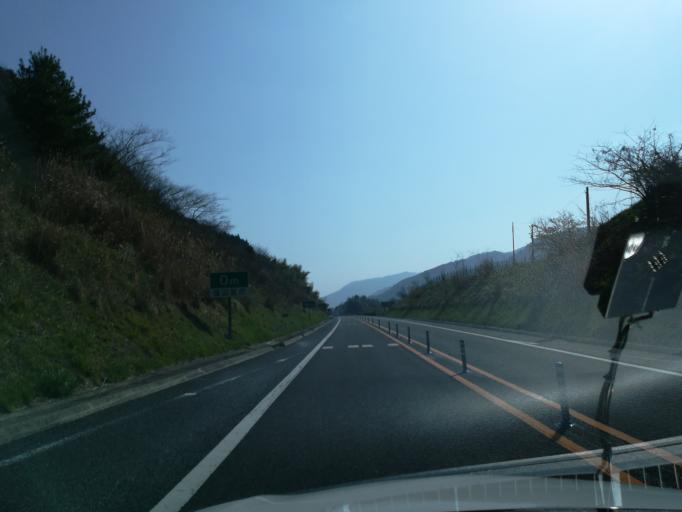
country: JP
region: Tokushima
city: Ikedacho
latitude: 34.0113
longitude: 133.7341
